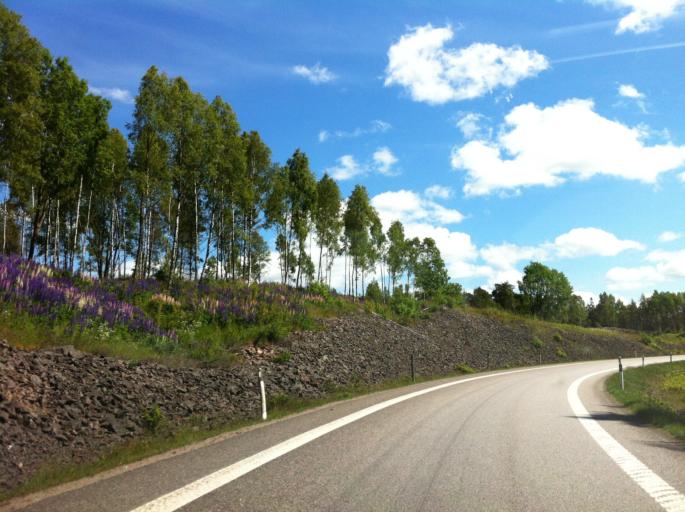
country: SE
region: Vaestra Goetaland
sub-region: Trollhattan
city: Trollhattan
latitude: 58.3360
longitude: 12.2831
